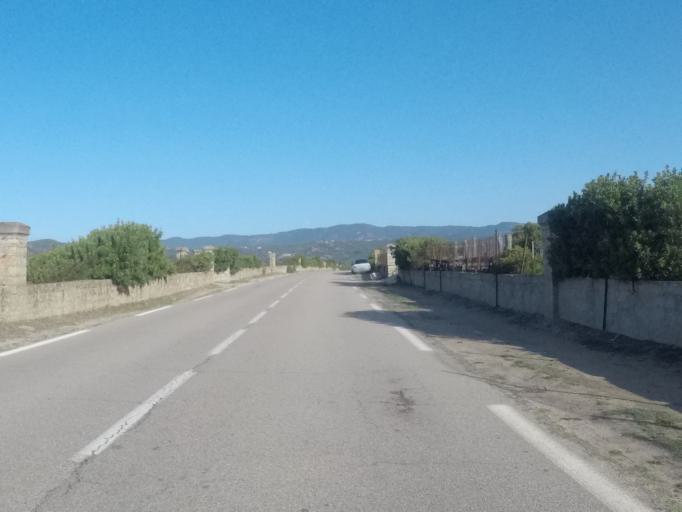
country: FR
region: Corsica
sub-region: Departement de la Corse-du-Sud
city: Propriano
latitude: 41.7050
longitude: 8.8332
